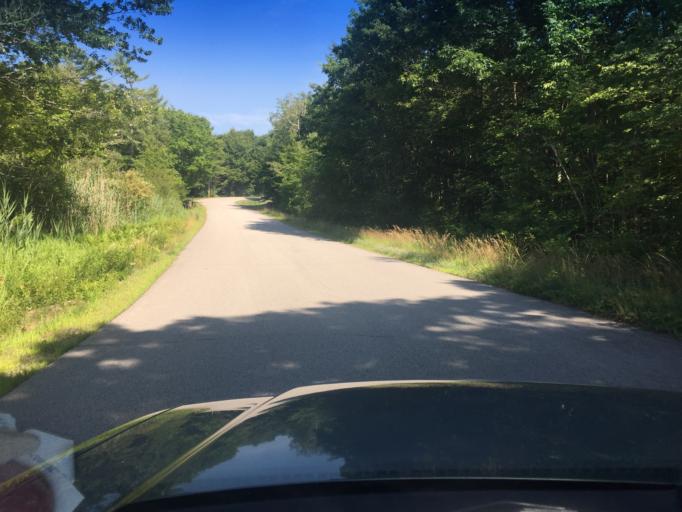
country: US
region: Maine
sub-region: York County
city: York Harbor
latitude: 43.1608
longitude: -70.6462
